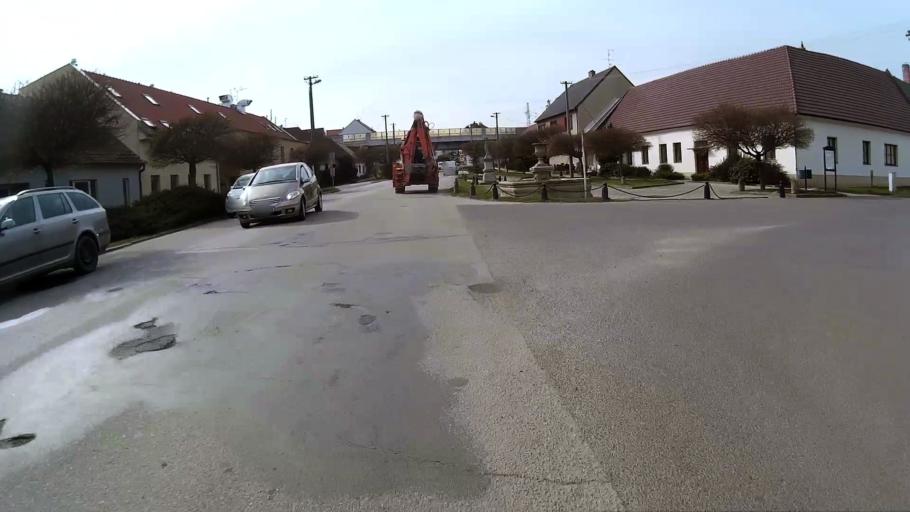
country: CZ
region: South Moravian
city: Rajhrad
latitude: 49.0890
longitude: 16.6070
